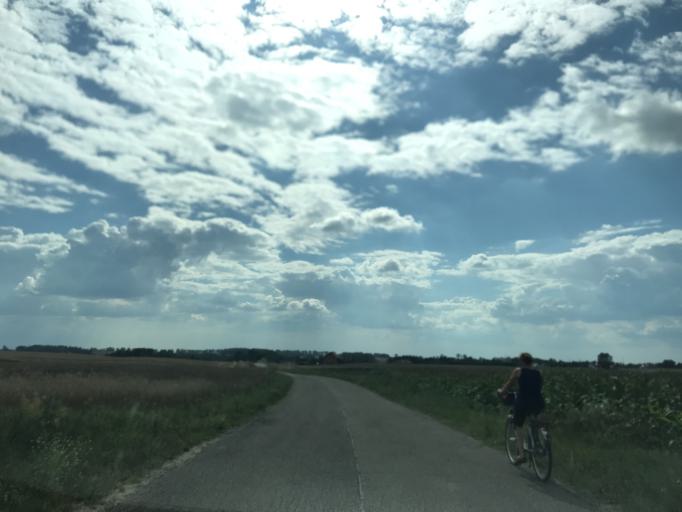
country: PL
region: Kujawsko-Pomorskie
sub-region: Powiat brodnicki
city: Brzozie
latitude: 53.3373
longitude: 19.6630
